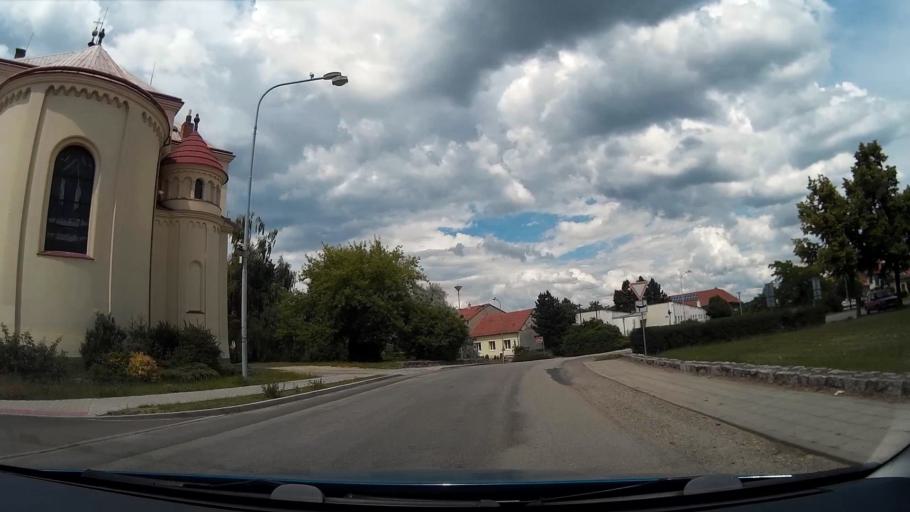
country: CZ
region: South Moravian
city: Orechov
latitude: 49.1097
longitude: 16.5260
